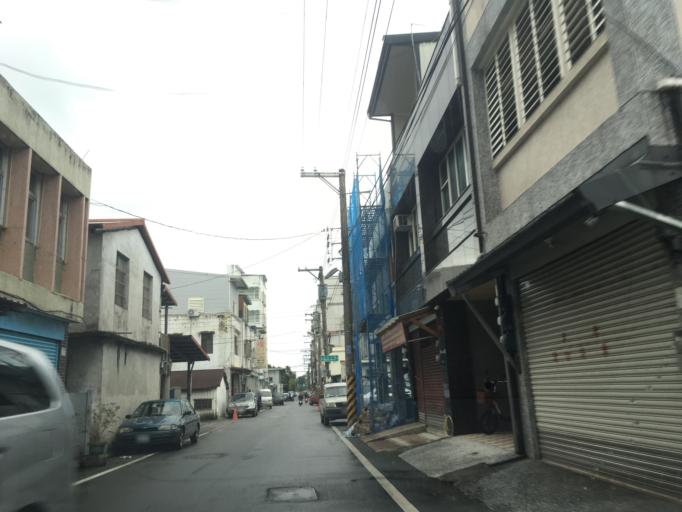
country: TW
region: Taiwan
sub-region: Hualien
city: Hualian
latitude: 23.9715
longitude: 121.5795
